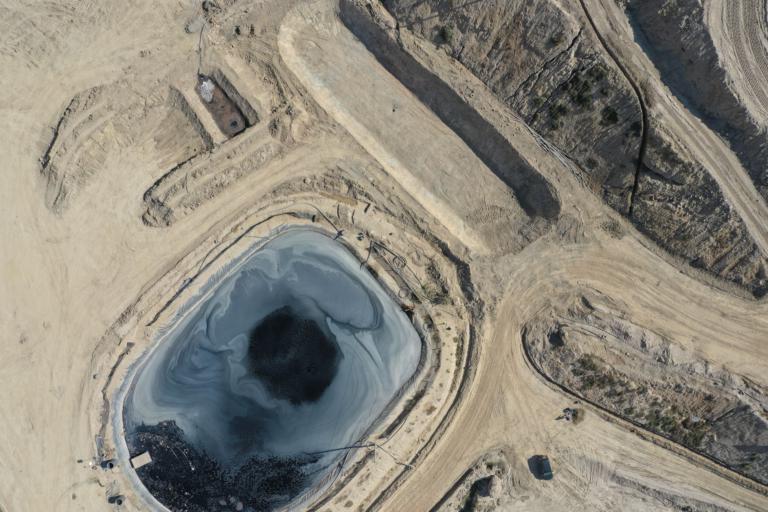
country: BO
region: La Paz
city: La Paz
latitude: -16.5582
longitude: -68.1278
